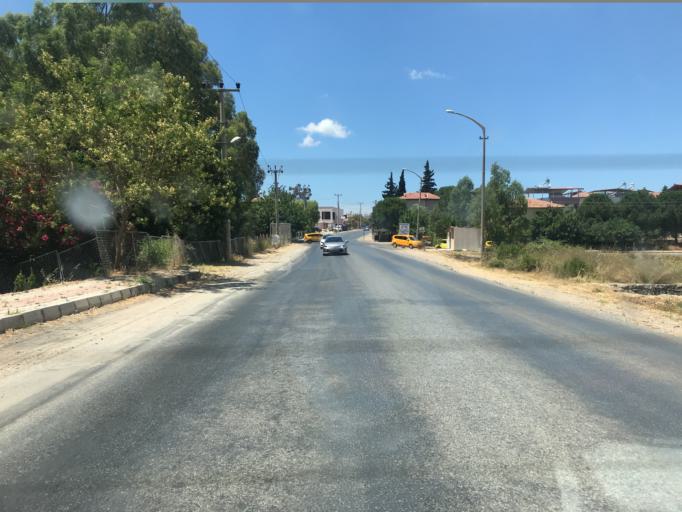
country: TR
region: Aydin
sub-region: Didim
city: Didim
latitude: 37.4130
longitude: 27.3889
